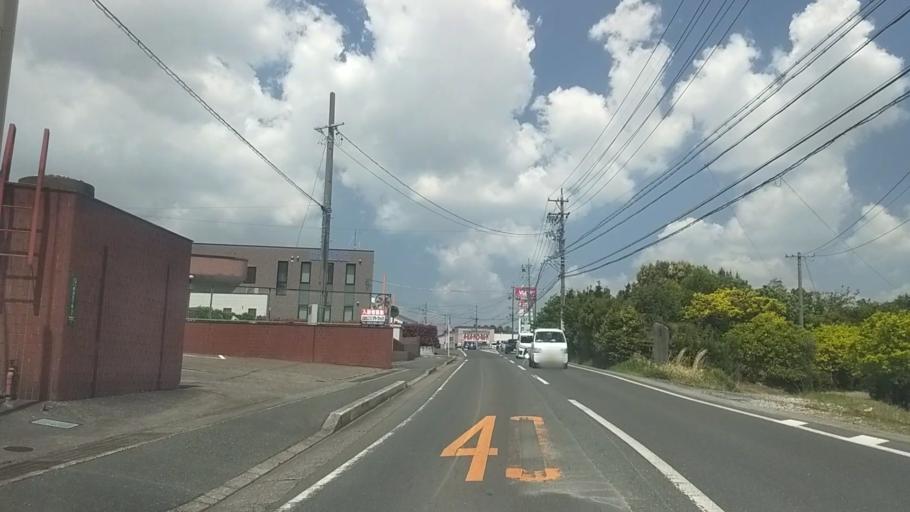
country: JP
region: Shizuoka
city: Hamamatsu
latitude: 34.7515
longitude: 137.7357
